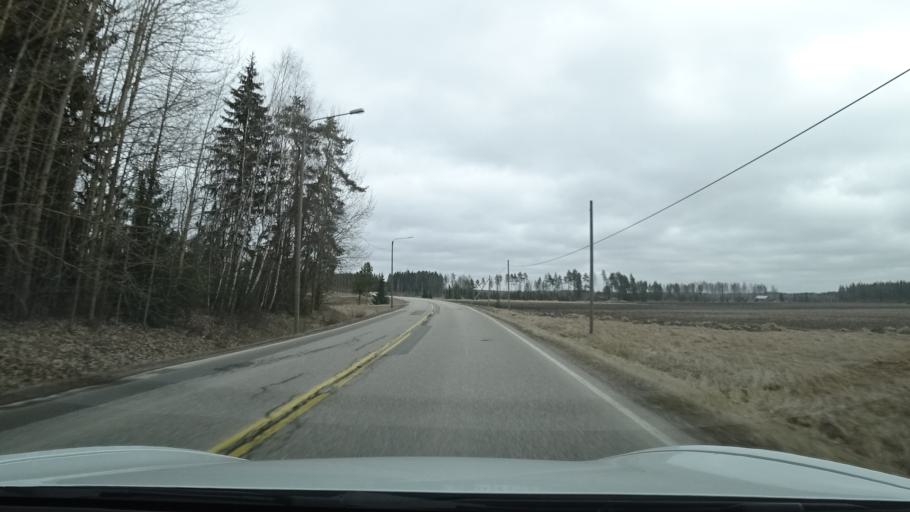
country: FI
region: Uusimaa
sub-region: Porvoo
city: Pukkila
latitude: 60.6567
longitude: 25.6862
